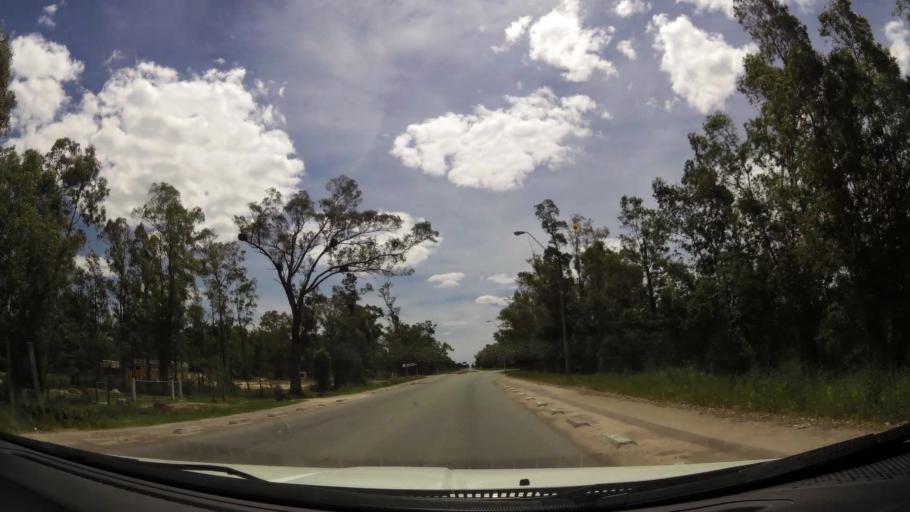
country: UY
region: San Jose
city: Delta del Tigre
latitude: -34.7358
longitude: -56.4457
